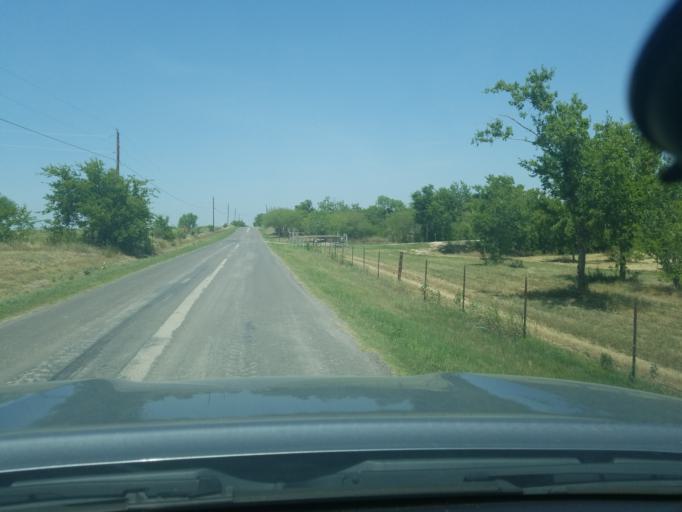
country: US
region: Texas
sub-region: Guadalupe County
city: Cibolo
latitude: 29.5720
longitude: -98.1889
